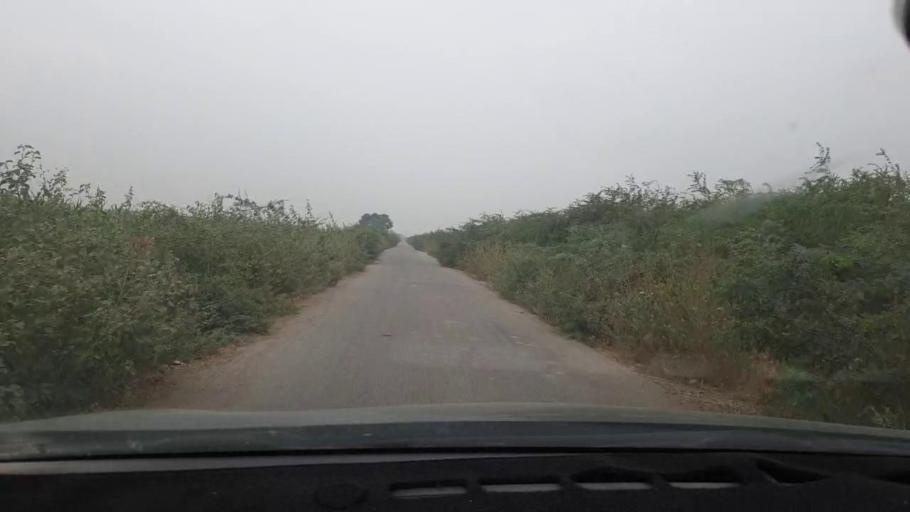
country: PK
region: Sindh
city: Malir Cantonment
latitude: 24.9250
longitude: 67.3304
